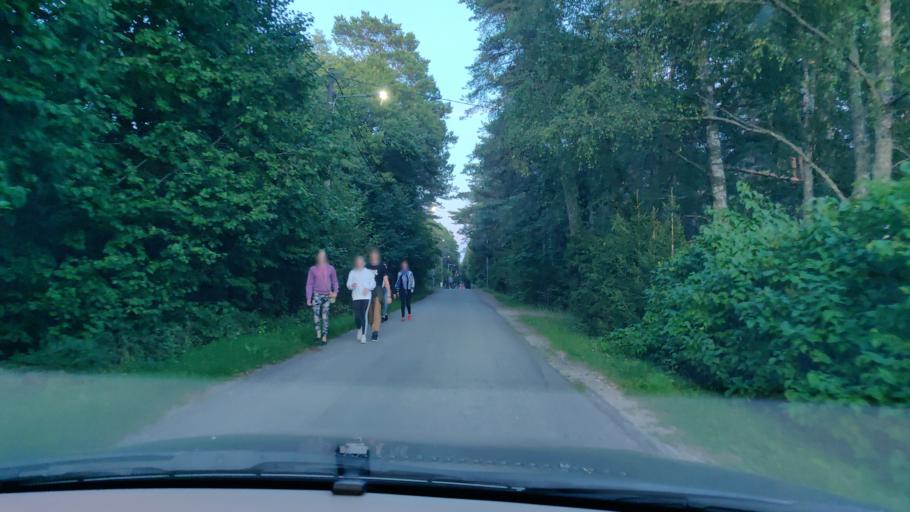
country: EE
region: Harju
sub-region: Keila linn
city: Keila
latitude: 59.3472
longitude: 24.2534
